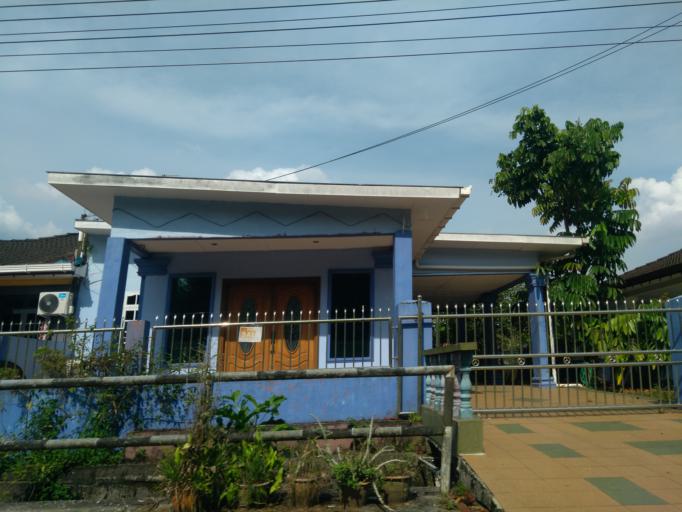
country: MY
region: Sarawak
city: Kuching
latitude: 1.5774
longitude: 110.2938
